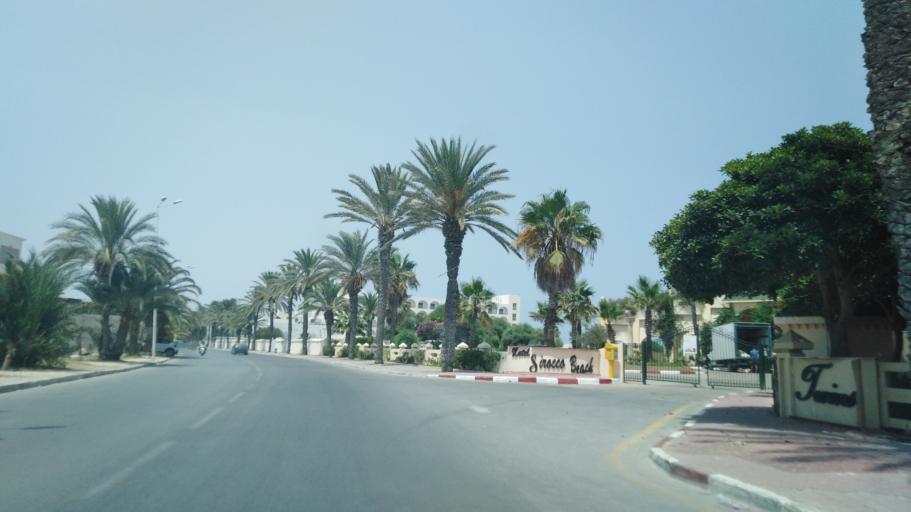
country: TN
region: Al Mahdiyah
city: Mahdia
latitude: 35.5150
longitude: 11.0466
